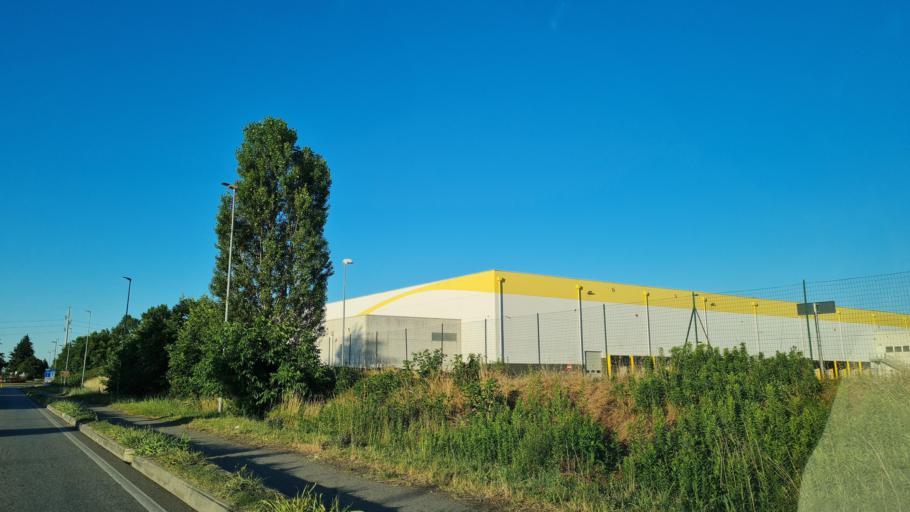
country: IT
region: Piedmont
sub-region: Provincia di Novara
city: Biandrate
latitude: 45.4614
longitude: 8.4644
